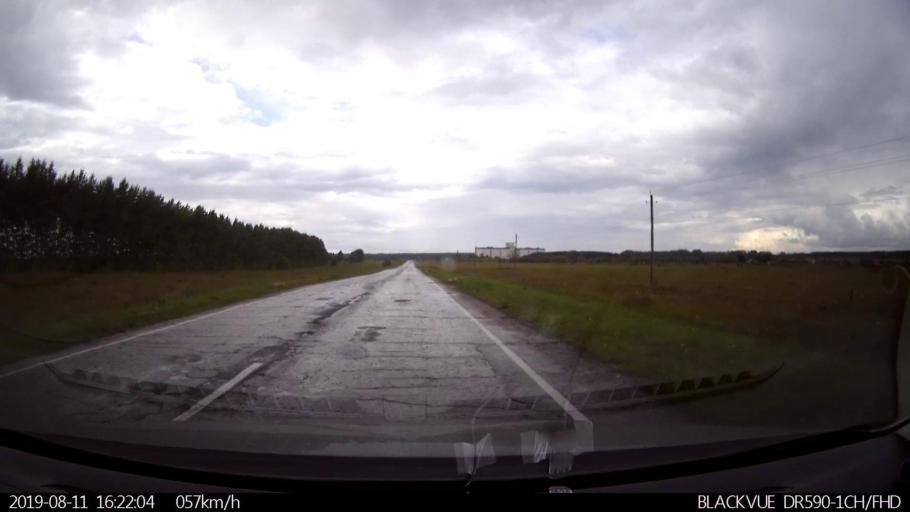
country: RU
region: Ulyanovsk
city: Mayna
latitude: 54.0849
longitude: 47.5948
